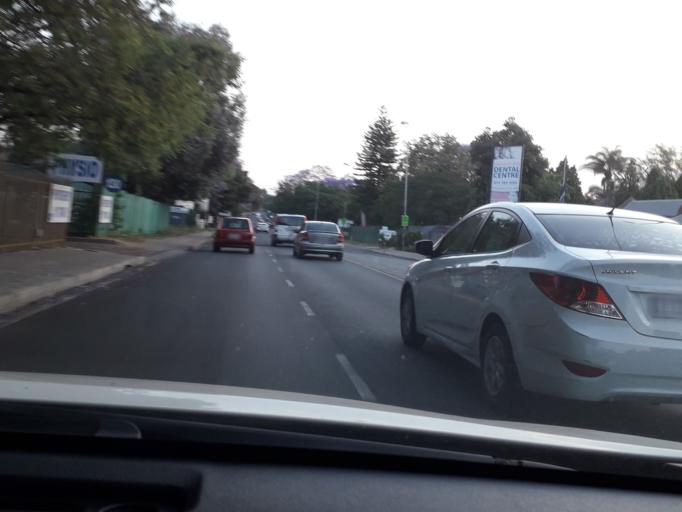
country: ZA
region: Gauteng
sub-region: City of Johannesburg Metropolitan Municipality
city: Johannesburg
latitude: -26.1041
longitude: 28.0021
